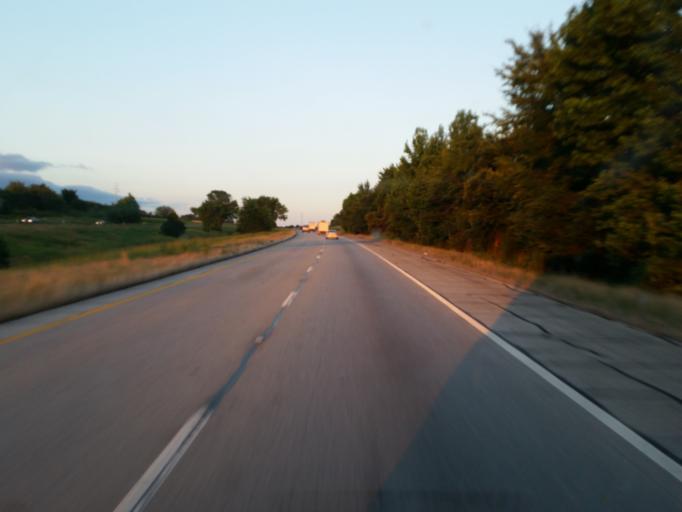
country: US
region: Texas
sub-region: Smith County
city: Hideaway
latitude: 32.4803
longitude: -95.4976
